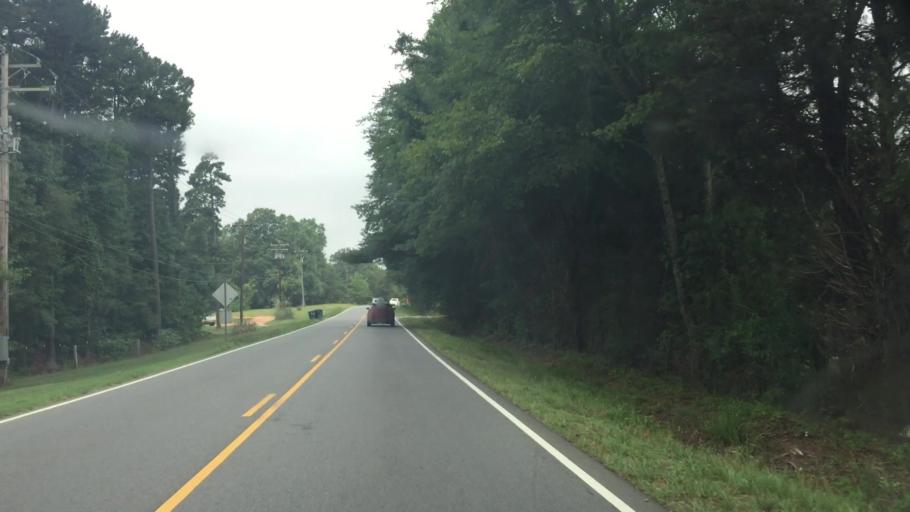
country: US
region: North Carolina
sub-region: Rowan County
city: Enochville
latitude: 35.4614
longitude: -80.7350
